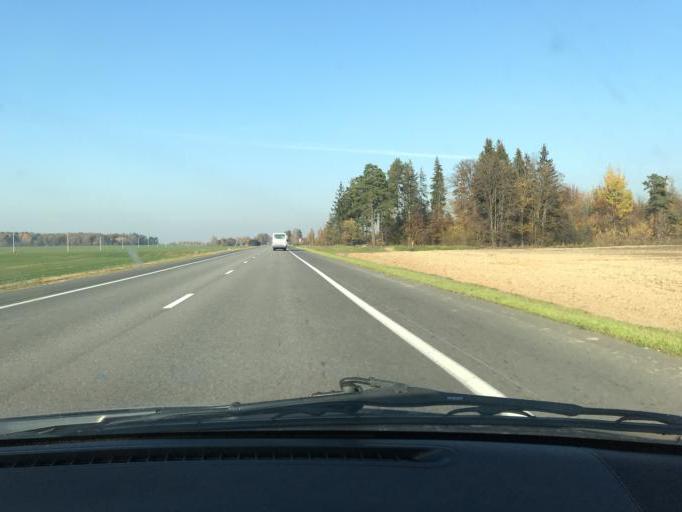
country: BY
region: Vitebsk
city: Balbasava
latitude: 54.3226
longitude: 30.4471
